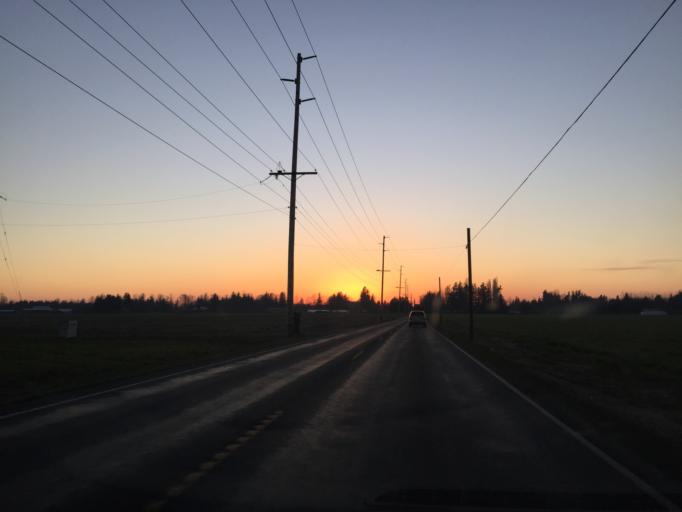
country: US
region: Washington
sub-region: Whatcom County
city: Nooksack
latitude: 48.9637
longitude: -122.3195
